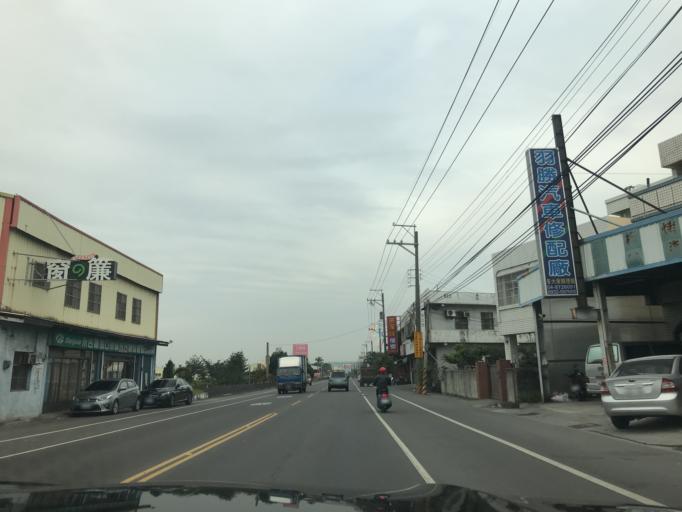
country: TW
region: Taiwan
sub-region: Nantou
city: Nantou
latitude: 23.9118
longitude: 120.5838
